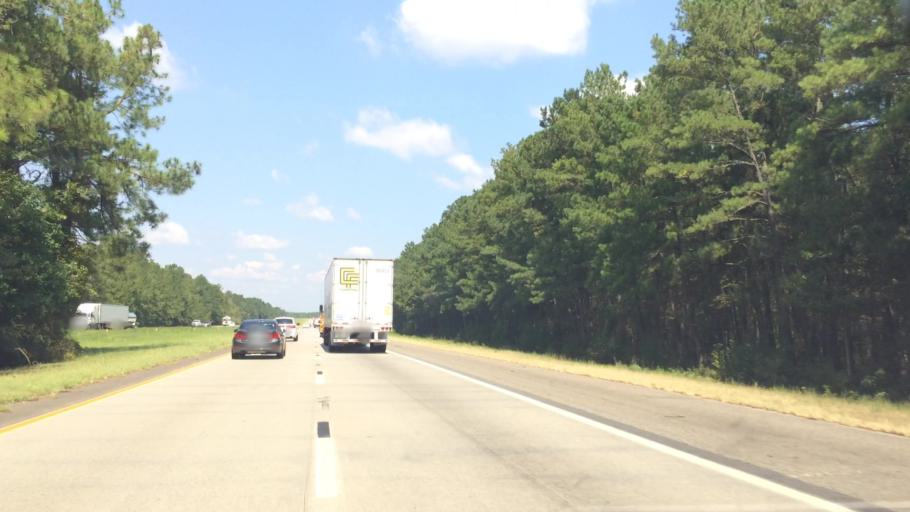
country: US
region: South Carolina
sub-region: Colleton County
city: Walterboro
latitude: 33.0249
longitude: -80.6657
